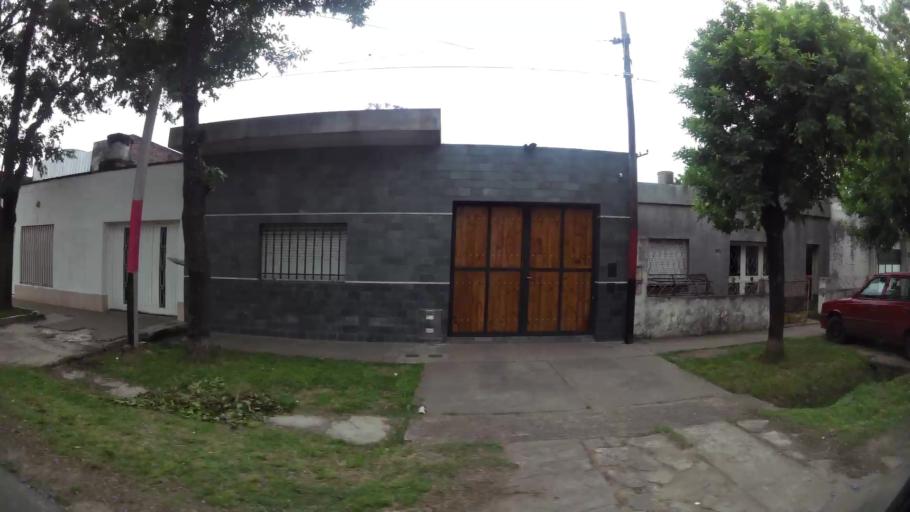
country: AR
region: Santa Fe
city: Gobernador Galvez
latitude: -33.0062
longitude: -60.6563
